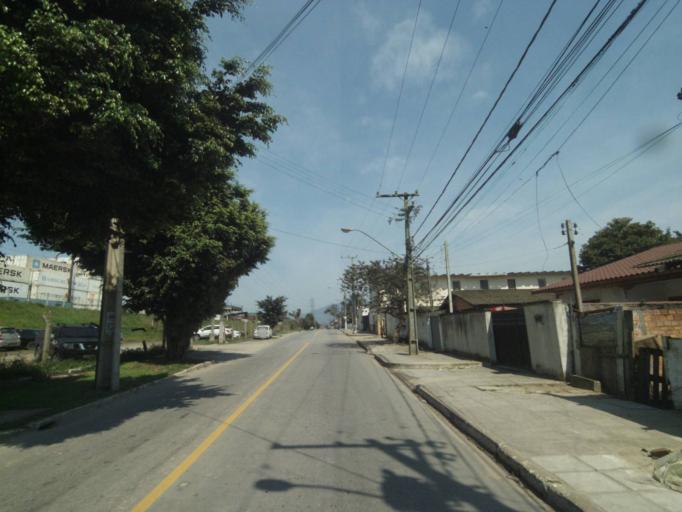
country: BR
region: Parana
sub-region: Paranagua
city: Paranagua
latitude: -25.5394
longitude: -48.5425
